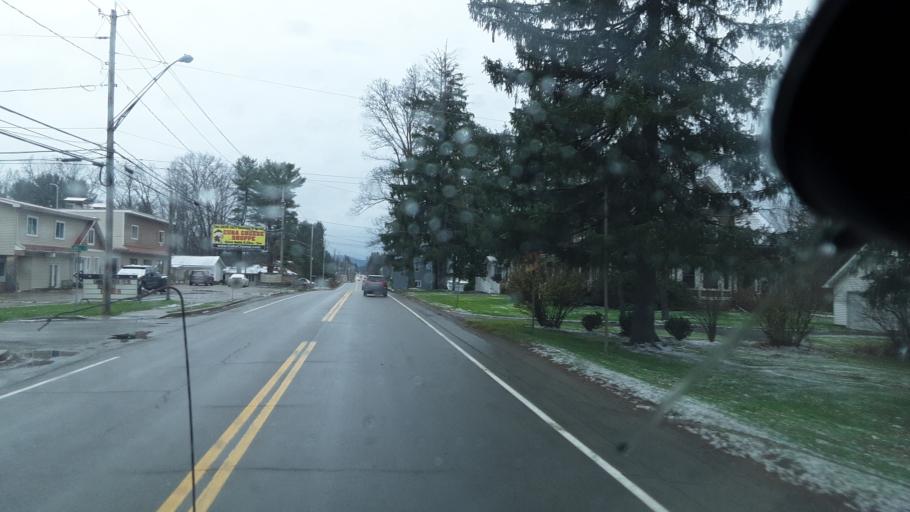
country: US
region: New York
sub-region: Cattaraugus County
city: Westons Mills
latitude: 42.0623
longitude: -78.3774
